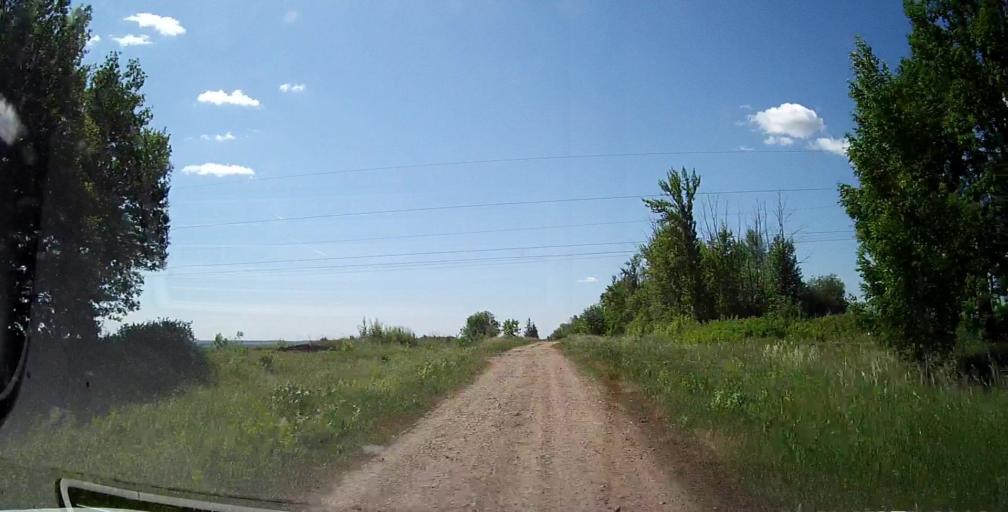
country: RU
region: Tula
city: Kurkino
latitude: 53.1785
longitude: 38.4850
